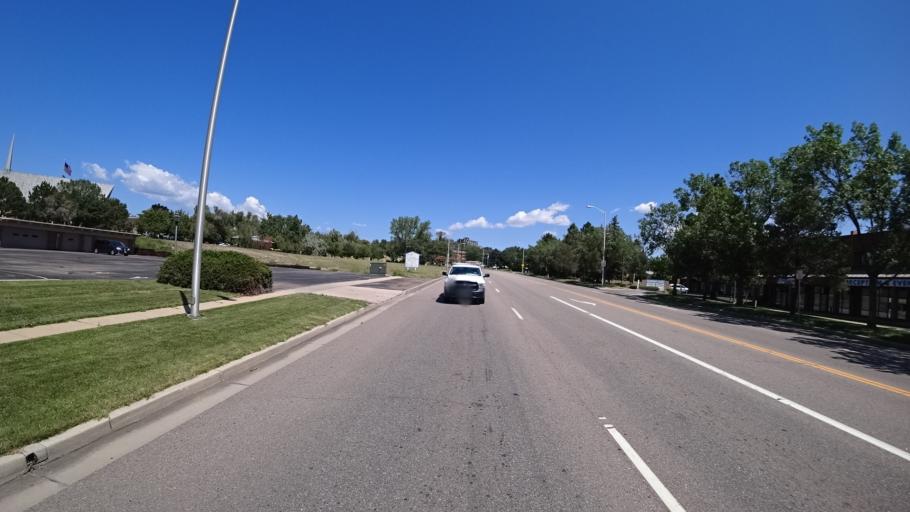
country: US
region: Colorado
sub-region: El Paso County
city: Colorado Springs
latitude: 38.8178
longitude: -104.7923
